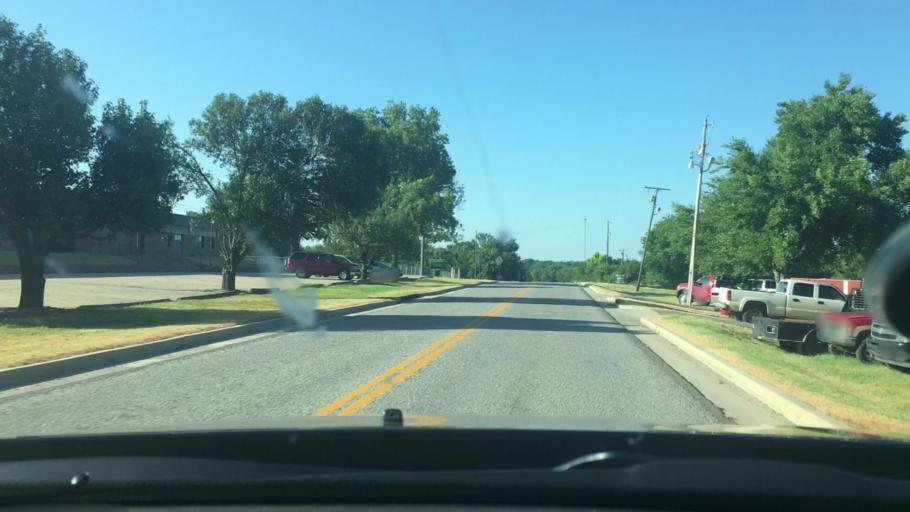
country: US
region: Oklahoma
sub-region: Murray County
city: Sulphur
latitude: 34.3990
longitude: -96.8271
